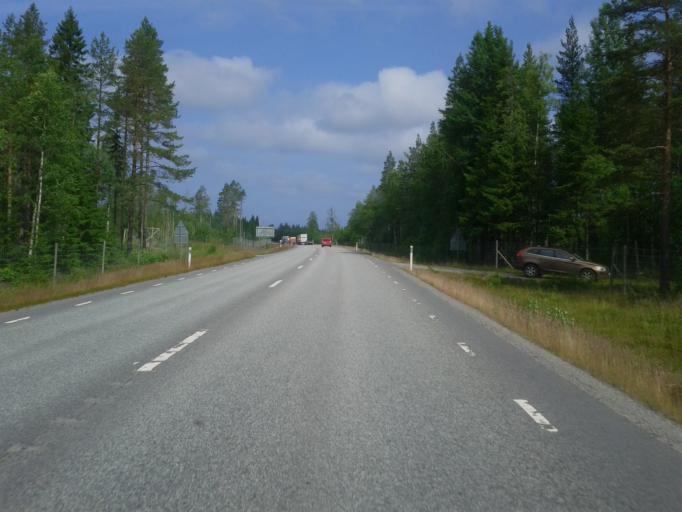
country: SE
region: Vaesterbotten
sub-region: Skelleftea Kommun
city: Burea
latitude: 64.4675
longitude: 21.2931
